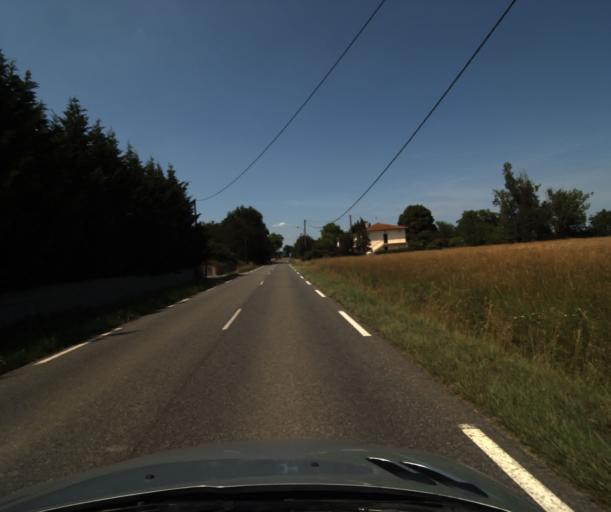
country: FR
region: Midi-Pyrenees
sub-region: Departement de la Haute-Garonne
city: Saint-Lys
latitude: 43.5242
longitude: 1.1726
